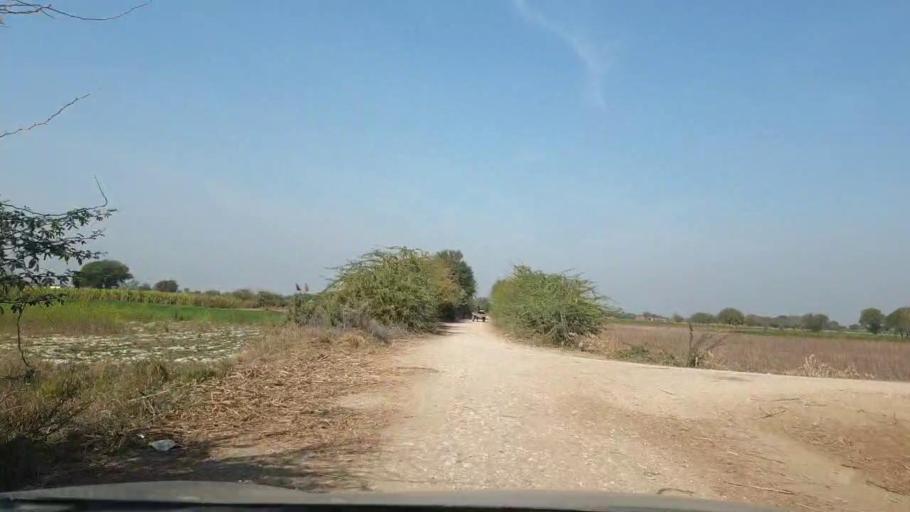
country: PK
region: Sindh
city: Berani
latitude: 25.7051
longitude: 68.7535
